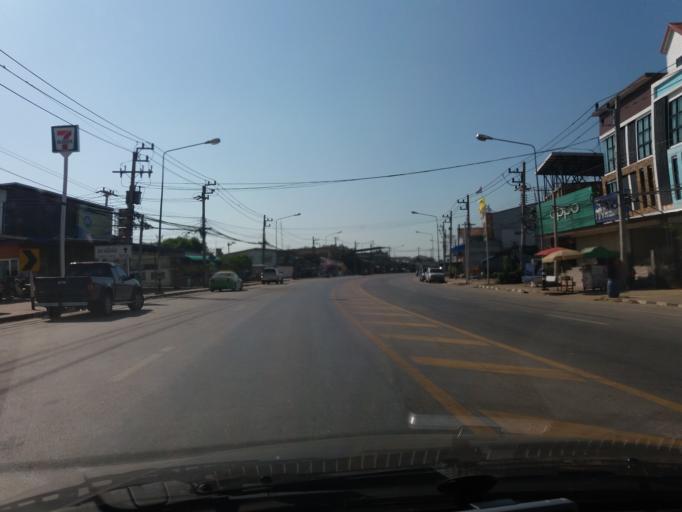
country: TH
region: Kamphaeng Phet
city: Khlong Khlung
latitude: 16.2327
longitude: 99.7332
